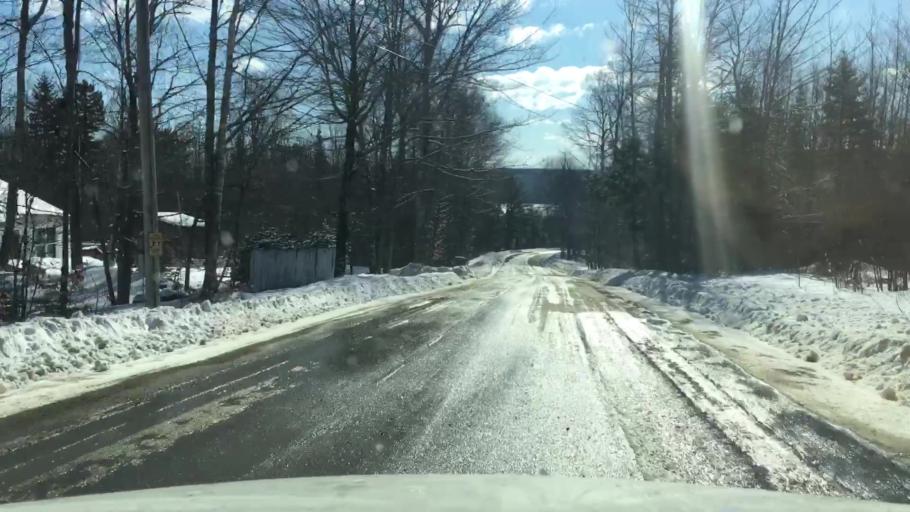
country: US
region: Maine
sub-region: Washington County
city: Calais
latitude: 45.0763
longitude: -67.5032
